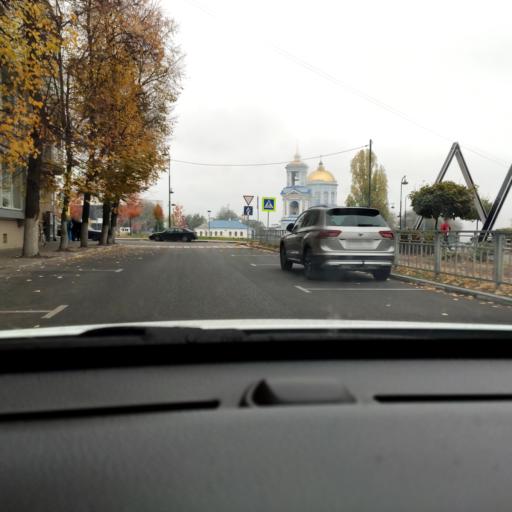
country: RU
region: Voronezj
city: Voronezh
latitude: 51.6641
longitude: 39.2110
